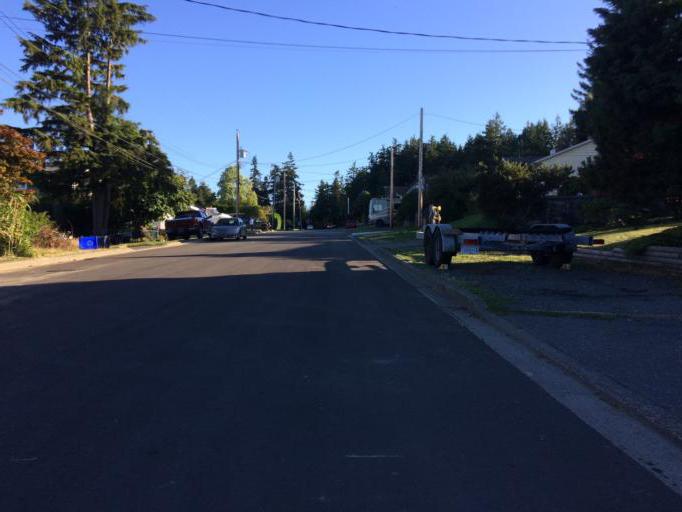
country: CA
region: British Columbia
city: Campbell River
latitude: 50.0178
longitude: -125.2382
